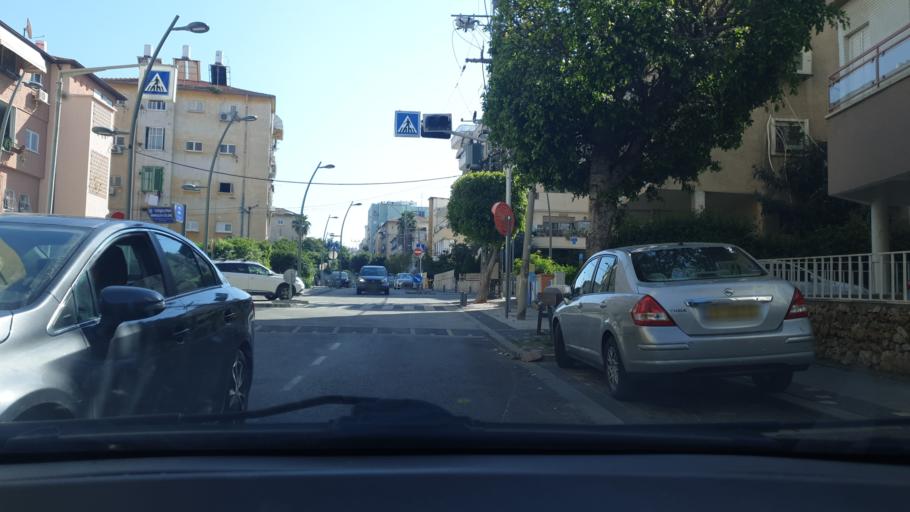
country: IL
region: Central District
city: Rishon LeZiyyon
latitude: 31.9693
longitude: 34.8063
